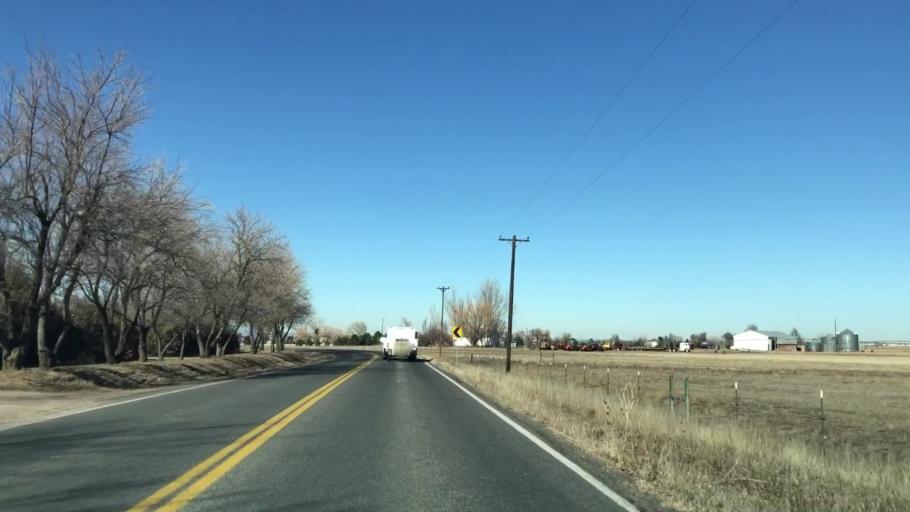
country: US
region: Colorado
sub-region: Weld County
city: Windsor
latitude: 40.4893
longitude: -104.9421
